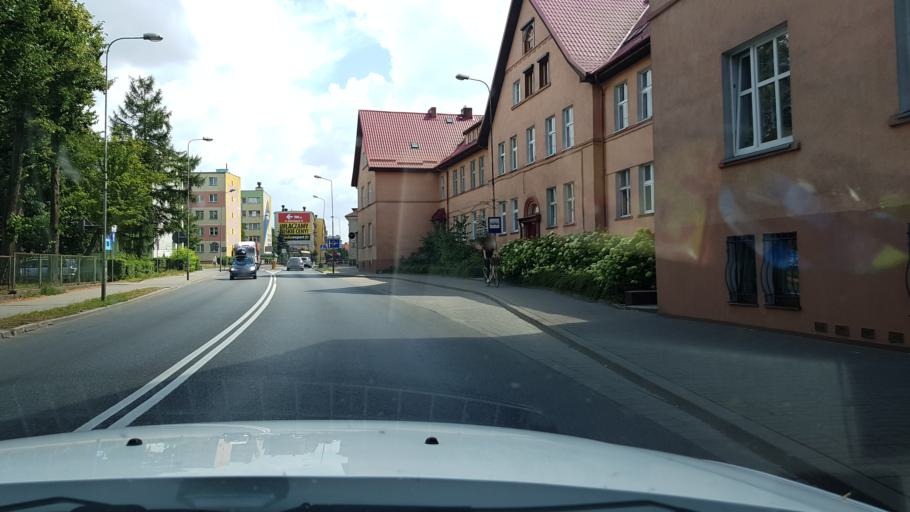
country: PL
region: West Pomeranian Voivodeship
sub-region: Powiat walecki
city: Walcz
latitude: 53.2764
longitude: 16.4733
